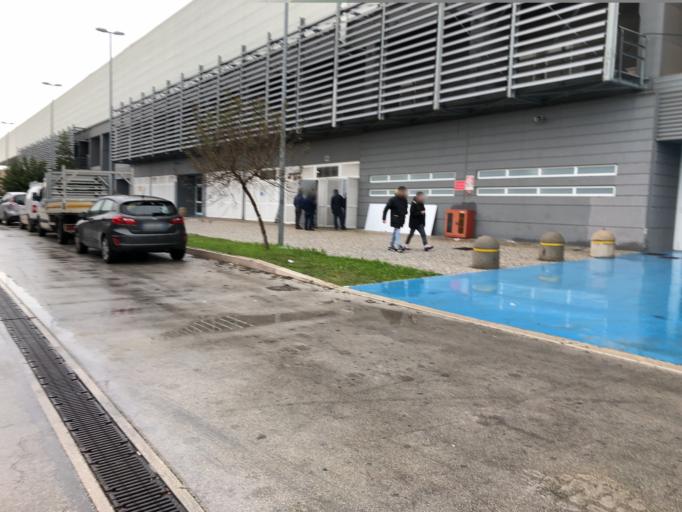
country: IT
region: Apulia
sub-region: Provincia di Bari
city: Bari
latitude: 41.1346
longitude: 16.8399
